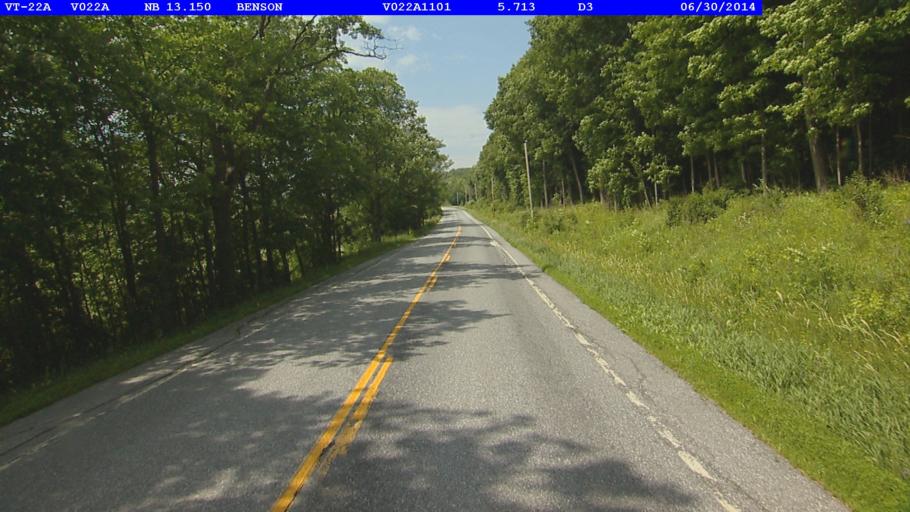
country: US
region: New York
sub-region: Essex County
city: Ticonderoga
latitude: 43.7497
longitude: -73.3084
